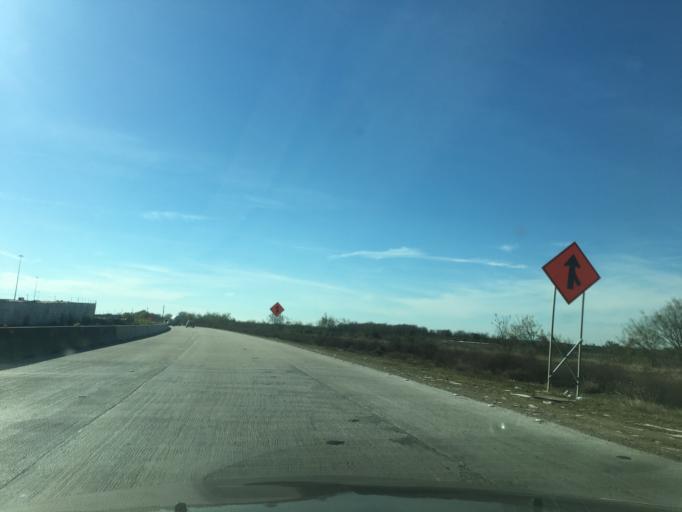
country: US
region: Texas
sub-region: Fort Bend County
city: Rosenberg
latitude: 29.5347
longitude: -95.8570
